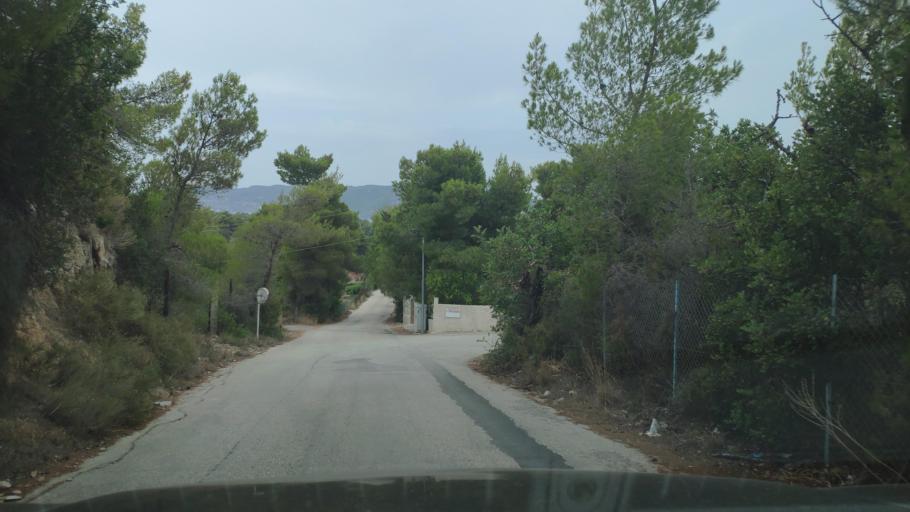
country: GR
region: Peloponnese
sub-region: Nomos Argolidos
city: Porto Cheli
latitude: 37.3093
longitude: 23.1473
